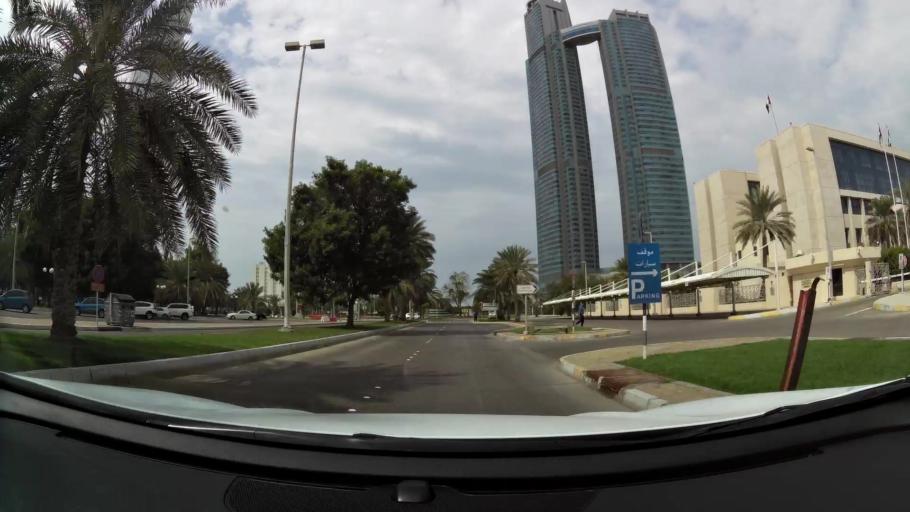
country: AE
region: Abu Dhabi
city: Abu Dhabi
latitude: 24.4614
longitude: 54.3285
